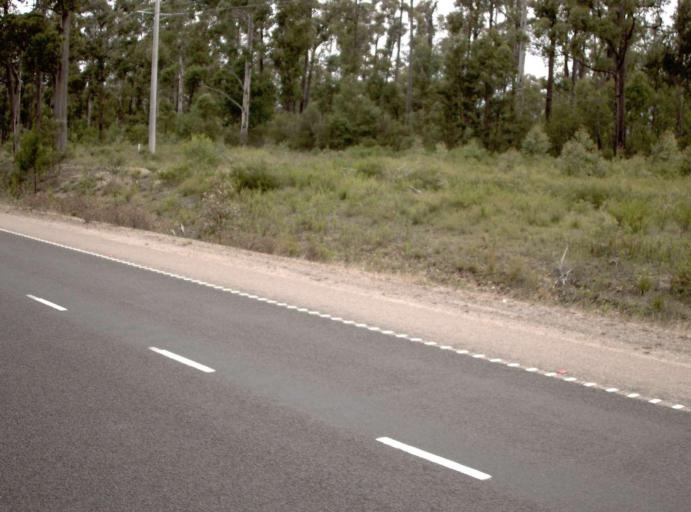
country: AU
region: Victoria
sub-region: East Gippsland
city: Lakes Entrance
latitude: -37.7179
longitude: 148.0774
